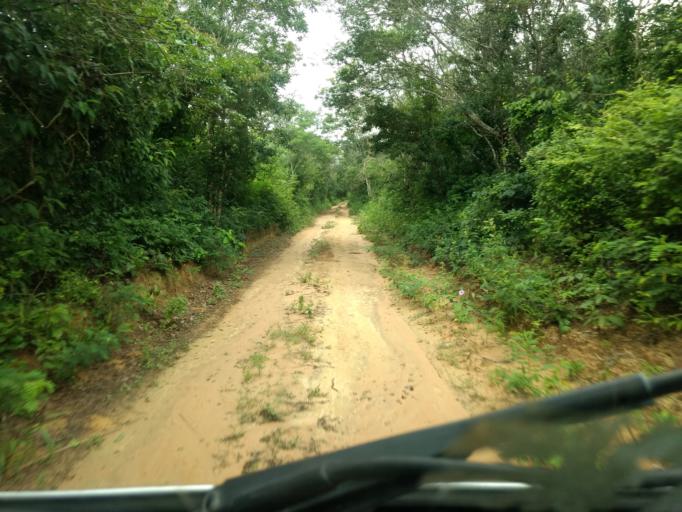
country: BR
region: Ceara
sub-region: Crateus
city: Crateus
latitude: -5.1767
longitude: -40.9367
